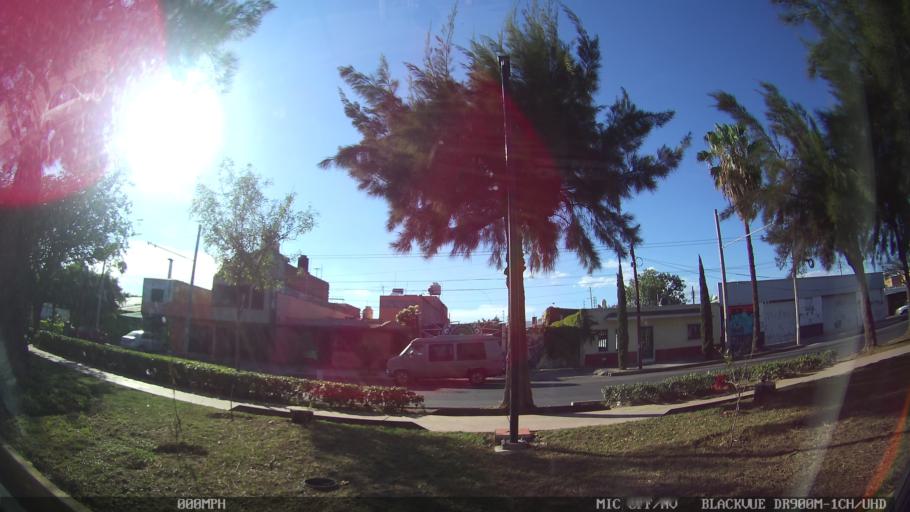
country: MX
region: Jalisco
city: Tlaquepaque
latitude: 20.6947
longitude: -103.3037
